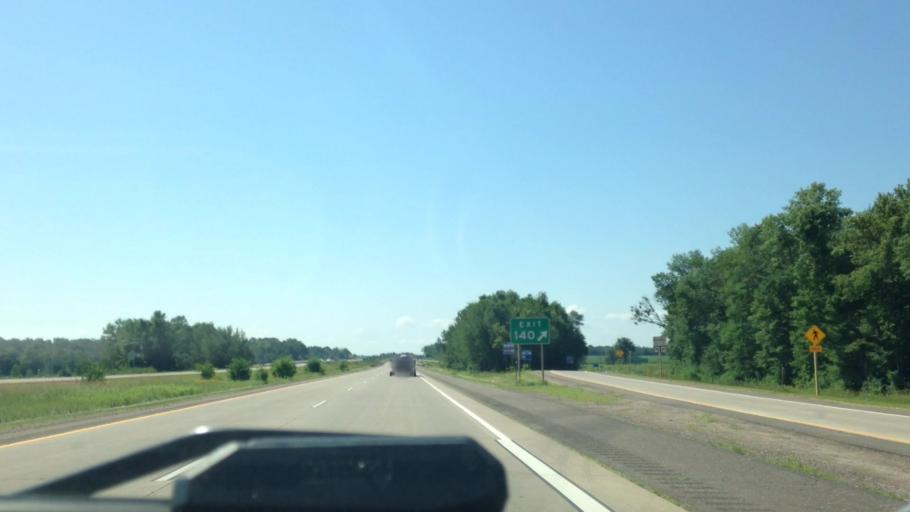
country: US
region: Wisconsin
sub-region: Barron County
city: Rice Lake
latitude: 45.4767
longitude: -91.7600
